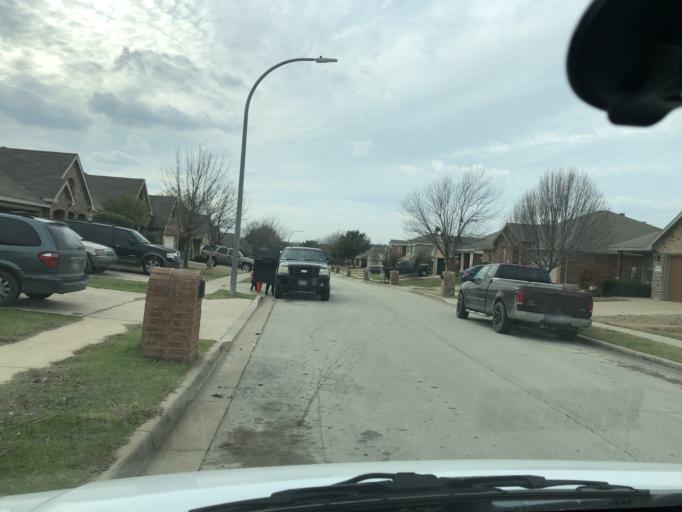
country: US
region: Texas
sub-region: Tarrant County
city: Saginaw
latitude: 32.9087
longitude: -97.3701
